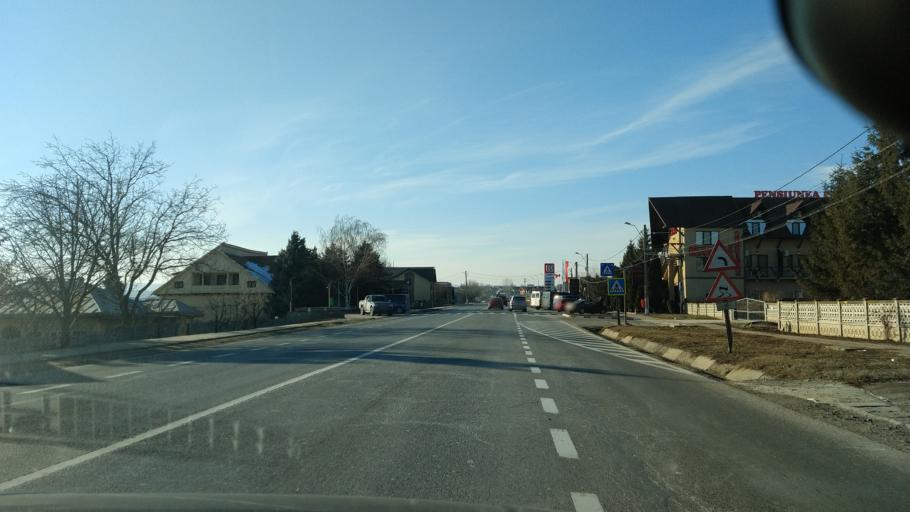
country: RO
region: Iasi
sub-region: Comuna Ion Neculce
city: Razboieni
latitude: 47.2177
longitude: 27.0359
